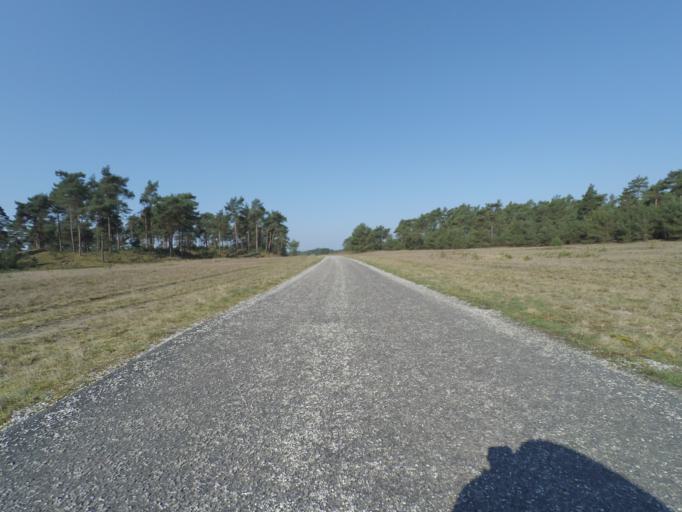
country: NL
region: Gelderland
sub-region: Gemeente Ede
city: Otterlo
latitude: 52.1181
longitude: 5.8175
